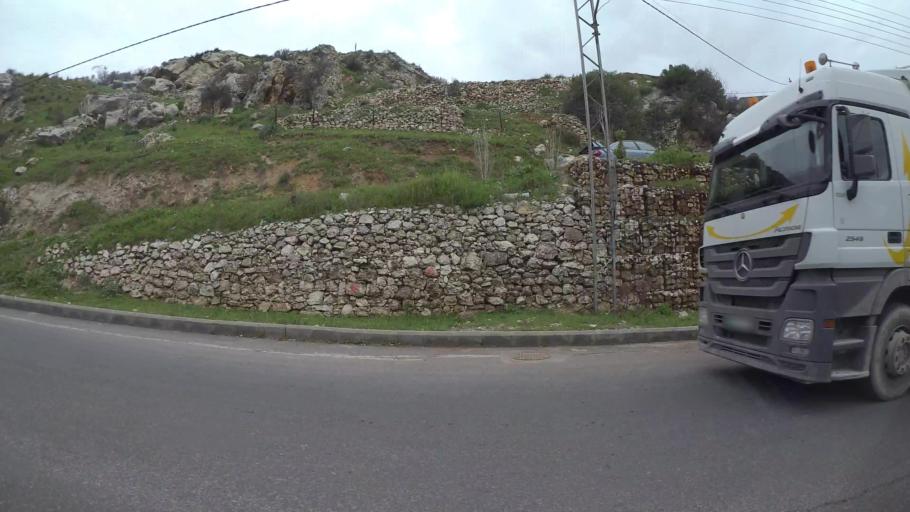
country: JO
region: Amman
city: Wadi as Sir
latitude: 31.9602
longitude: 35.8113
